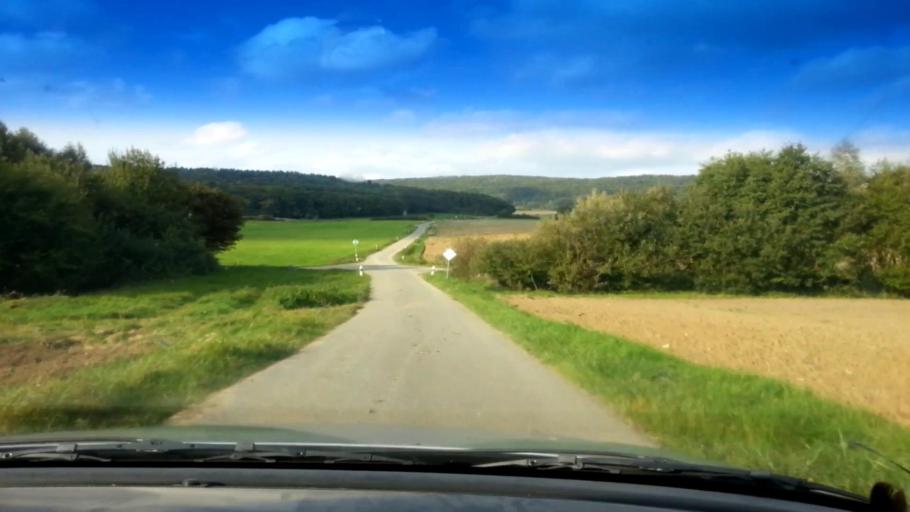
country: DE
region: Bavaria
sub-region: Upper Franconia
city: Schesslitz
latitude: 49.9958
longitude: 11.0467
